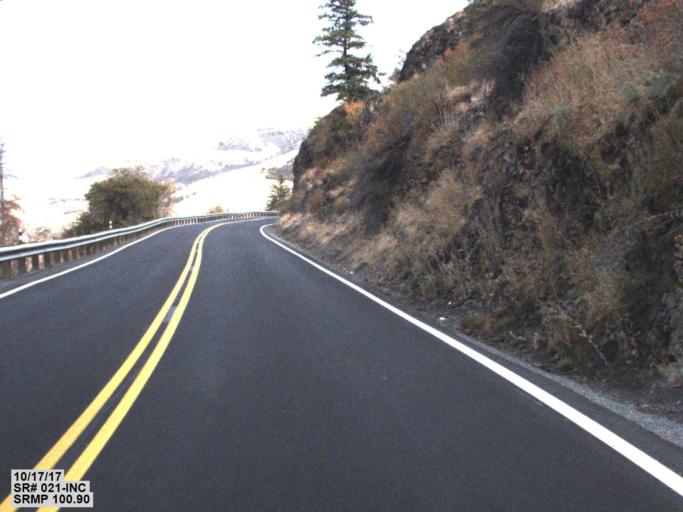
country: US
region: Washington
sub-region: Okanogan County
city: Coulee Dam
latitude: 47.8701
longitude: -118.7226
